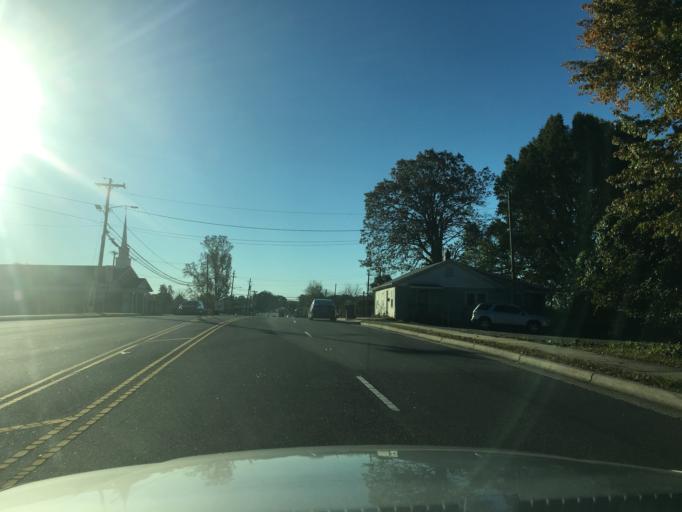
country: US
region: North Carolina
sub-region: Catawba County
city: Hickory
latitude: 35.7296
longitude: -81.3254
